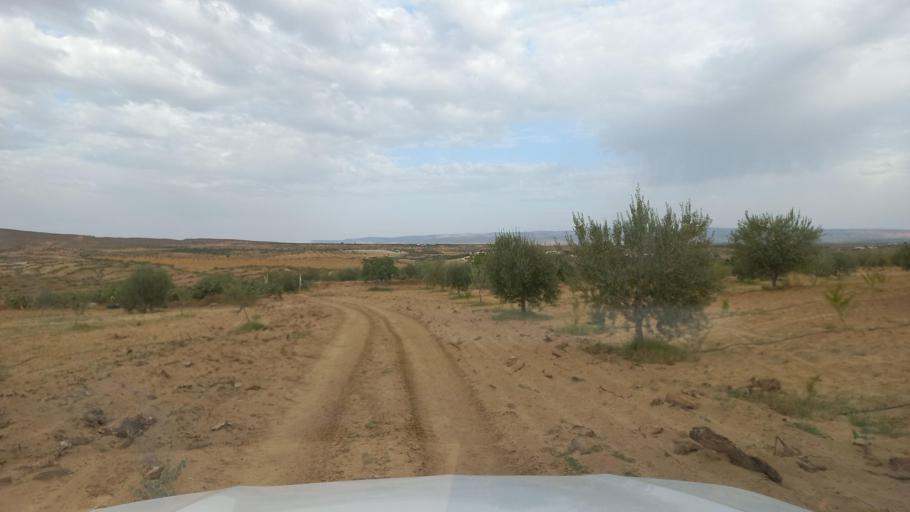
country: TN
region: Al Qasrayn
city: Kasserine
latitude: 35.1944
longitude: 9.0461
